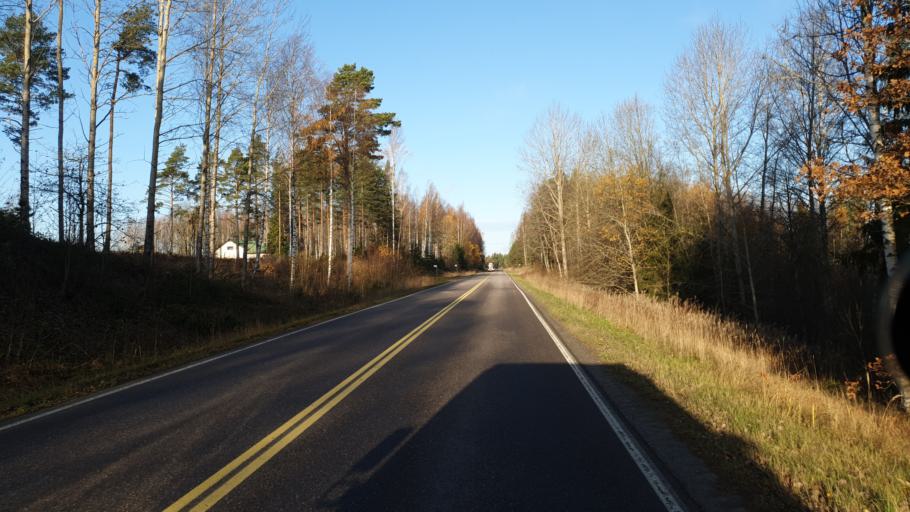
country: FI
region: Uusimaa
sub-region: Helsinki
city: Siuntio
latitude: 60.1927
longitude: 24.1994
